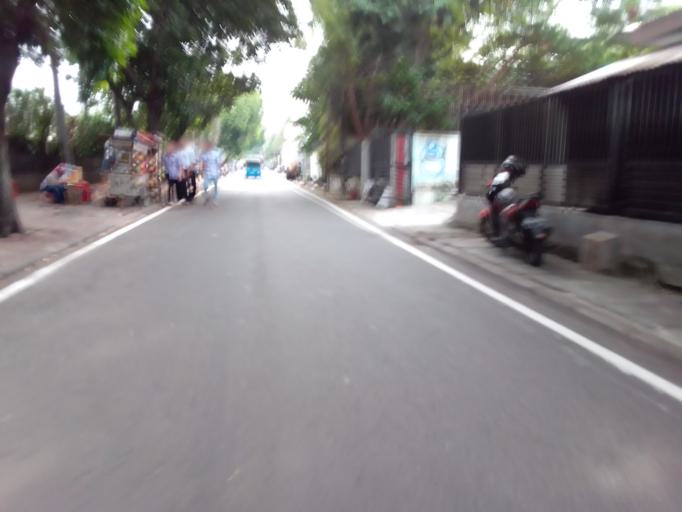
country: ID
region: Jakarta Raya
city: Jakarta
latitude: -6.1776
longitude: 106.8185
